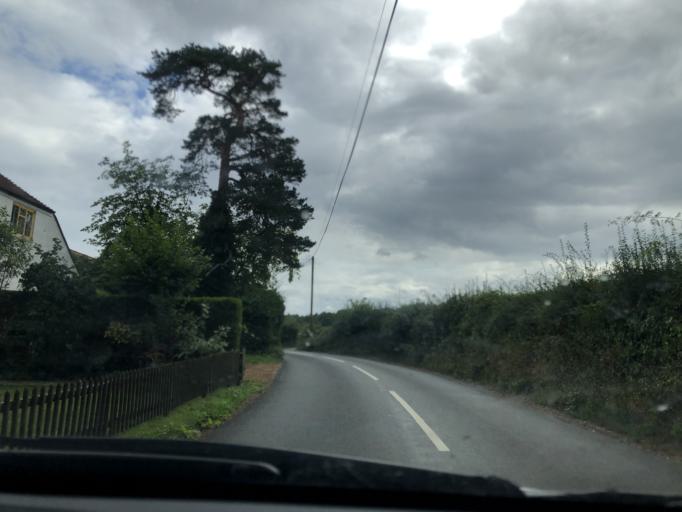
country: GB
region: England
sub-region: Kent
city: Edenbridge
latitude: 51.2250
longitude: 0.0913
